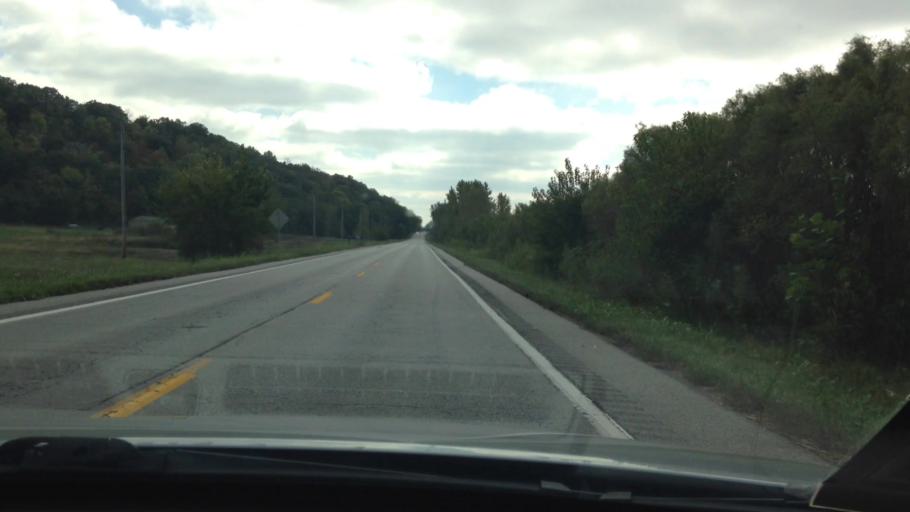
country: US
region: Kansas
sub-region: Leavenworth County
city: Lansing
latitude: 39.2509
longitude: -94.8060
